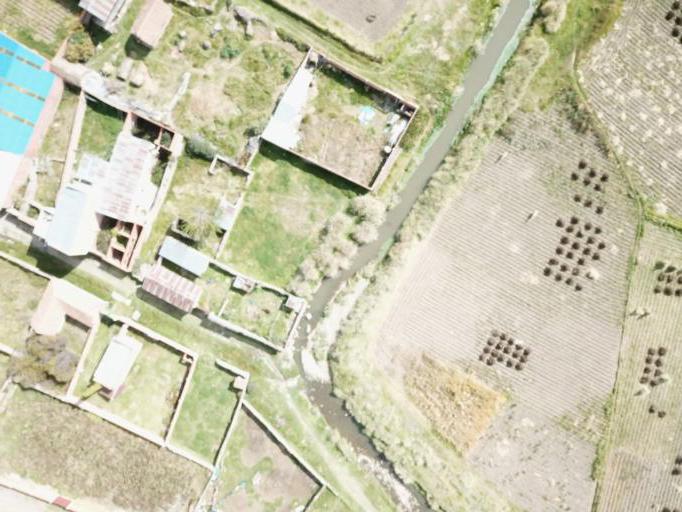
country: BO
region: La Paz
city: Achacachi
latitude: -16.0549
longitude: -68.8156
